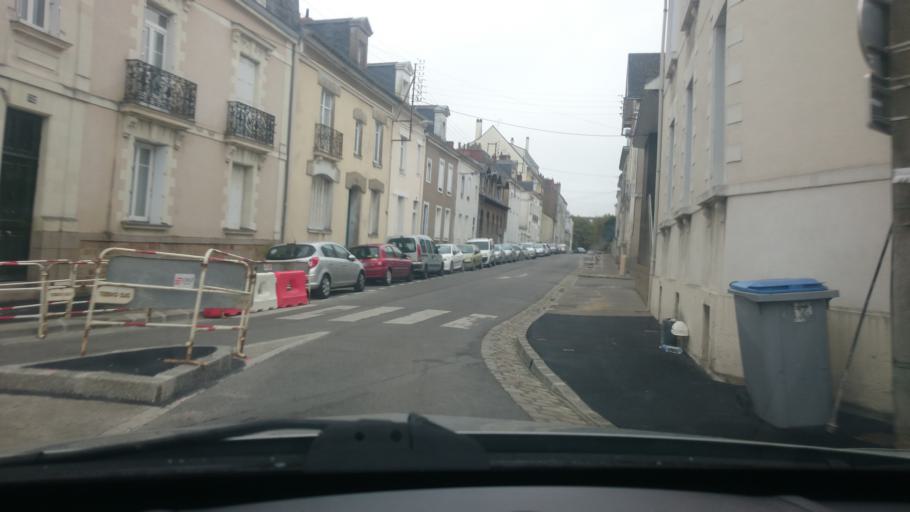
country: FR
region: Pays de la Loire
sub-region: Departement de la Loire-Atlantique
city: Nantes
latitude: 47.2167
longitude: -1.5754
